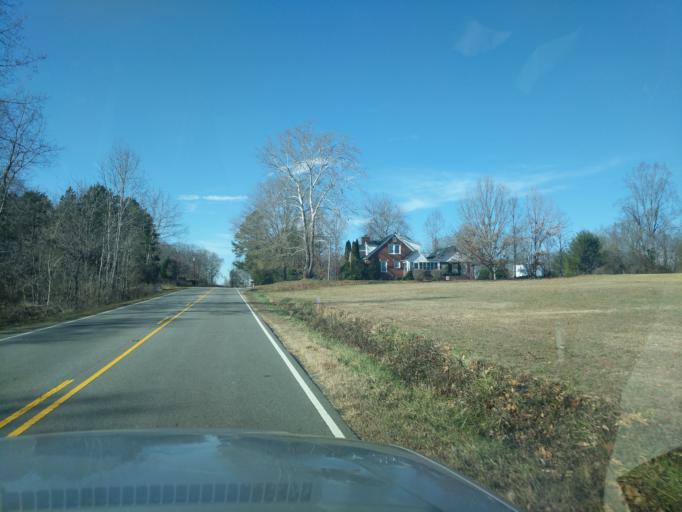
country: US
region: North Carolina
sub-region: Rutherford County
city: Spindale
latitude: 35.3286
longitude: -81.9523
